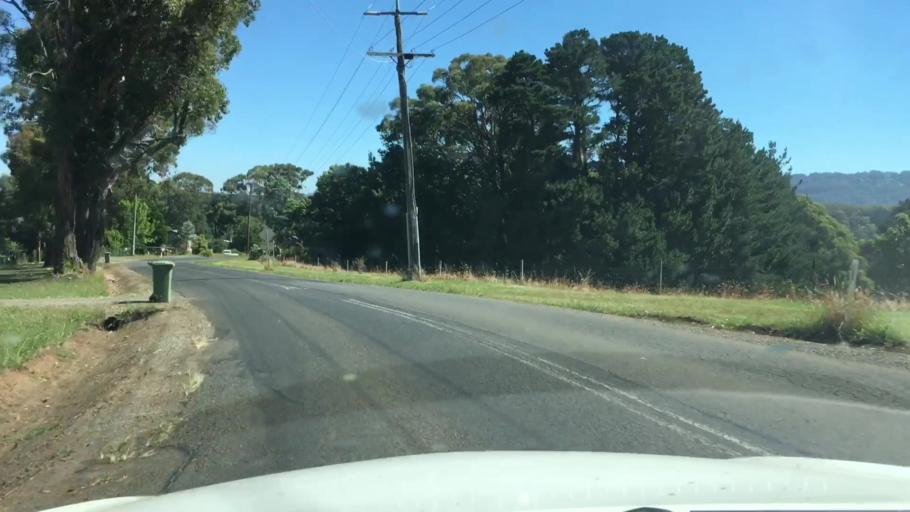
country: AU
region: Victoria
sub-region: Yarra Ranges
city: Mount Evelyn
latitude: -37.8135
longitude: 145.4232
